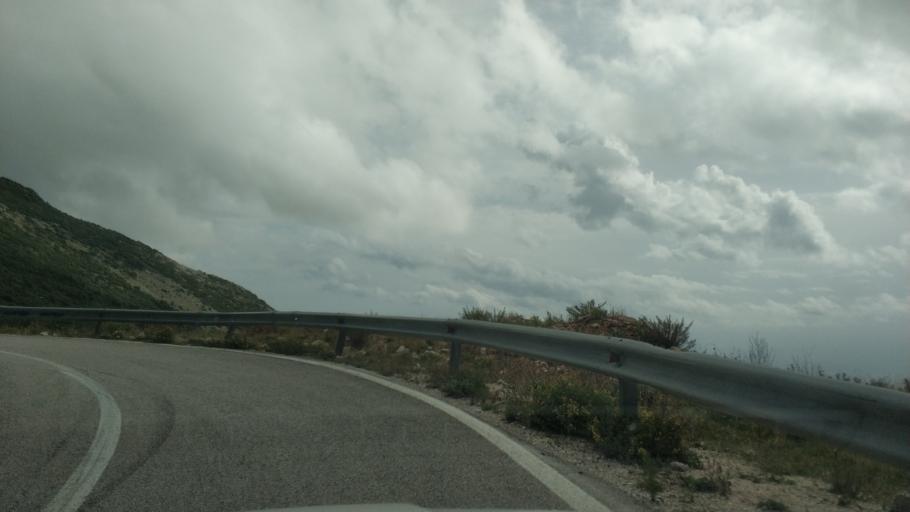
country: AL
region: Vlore
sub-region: Rrethi i Vlores
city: Vranisht
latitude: 40.1853
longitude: 19.6101
